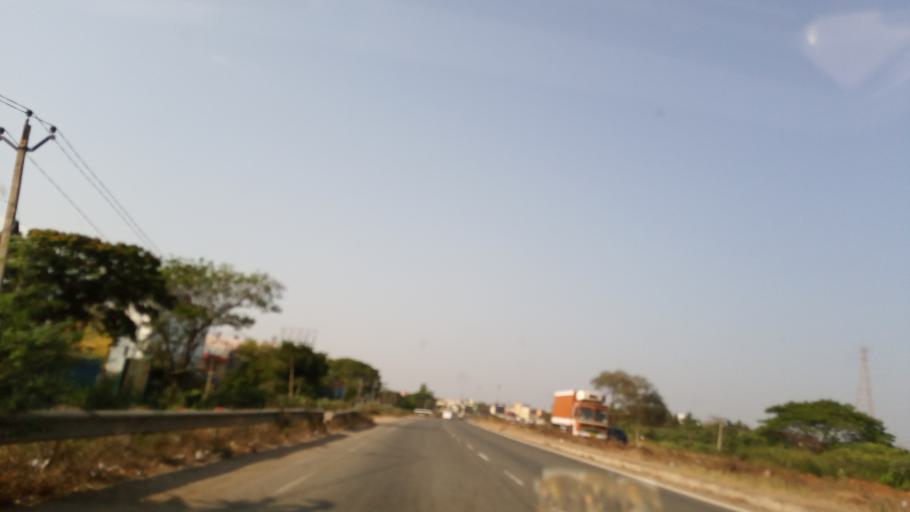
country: IN
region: Tamil Nadu
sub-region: Kancheepuram
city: Sriperumbudur
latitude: 12.9712
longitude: 79.9551
